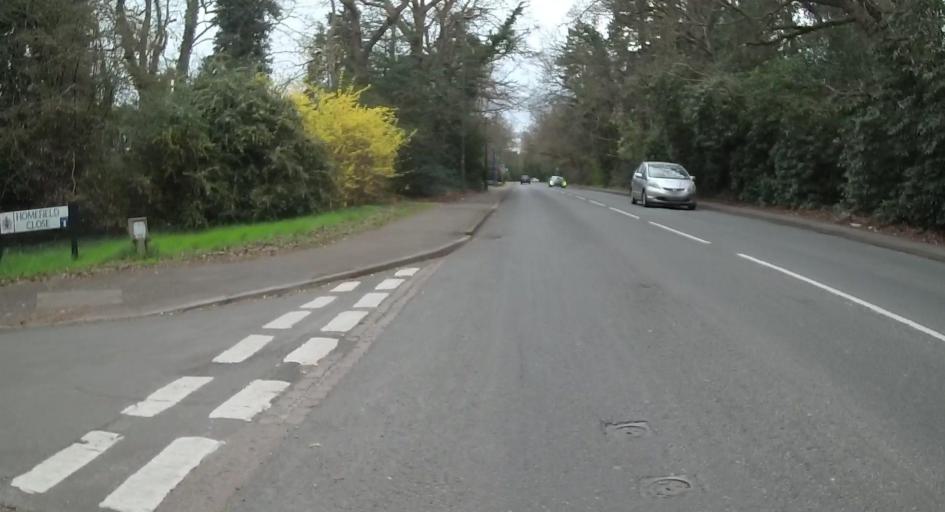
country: GB
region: England
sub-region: Surrey
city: West Byfleet
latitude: 51.3421
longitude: -0.5185
